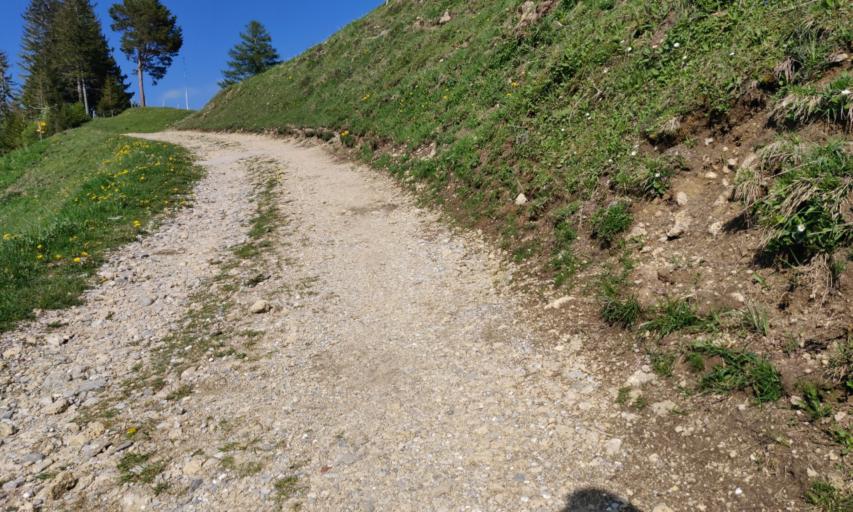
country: CH
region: Fribourg
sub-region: Gruyere District
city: Vuadens
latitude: 46.5668
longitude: 7.0237
